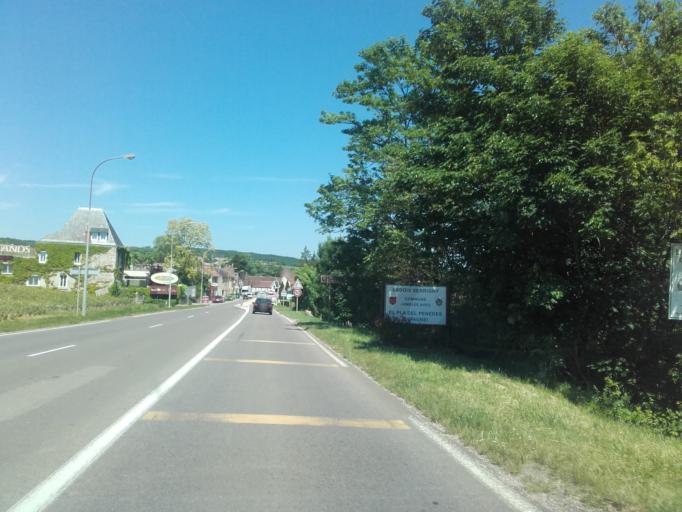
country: FR
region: Bourgogne
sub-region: Departement de la Cote-d'Or
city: Beaune
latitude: 47.0697
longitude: 4.8729
